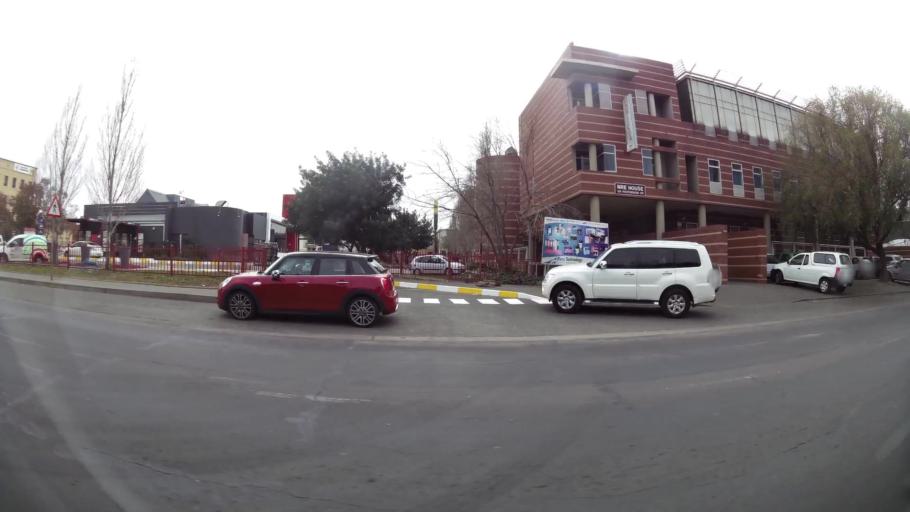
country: ZA
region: Orange Free State
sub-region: Mangaung Metropolitan Municipality
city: Bloemfontein
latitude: -29.1111
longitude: 26.2064
